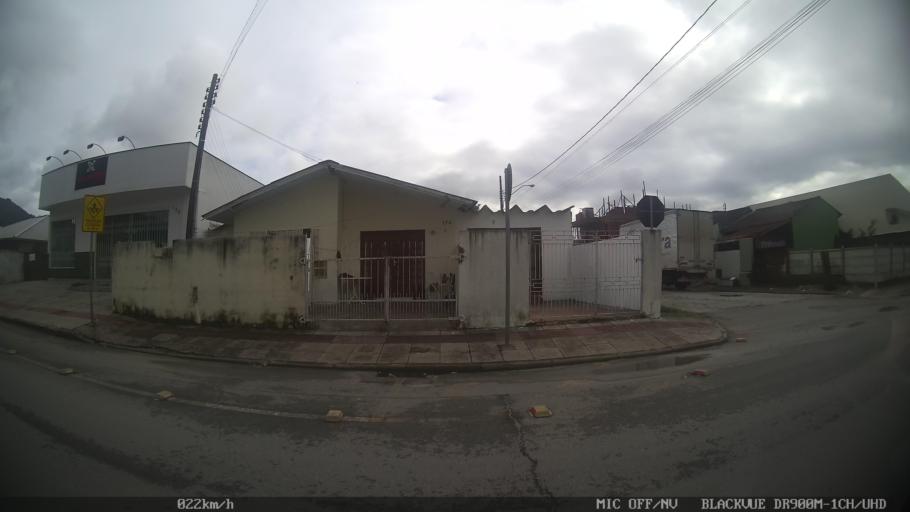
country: BR
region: Santa Catarina
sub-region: Biguacu
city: Biguacu
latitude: -27.5145
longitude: -48.6448
